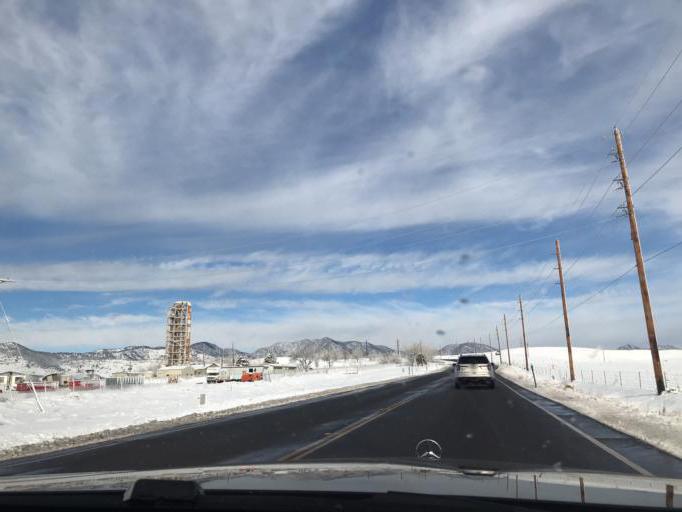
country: US
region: Colorado
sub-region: Boulder County
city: Superior
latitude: 39.8595
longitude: -105.1938
